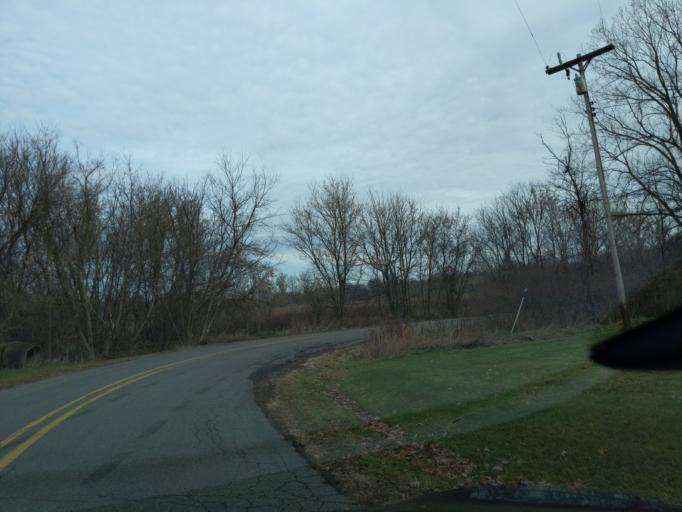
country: US
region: Michigan
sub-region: Ingham County
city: Leslie
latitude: 42.4652
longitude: -84.5099
